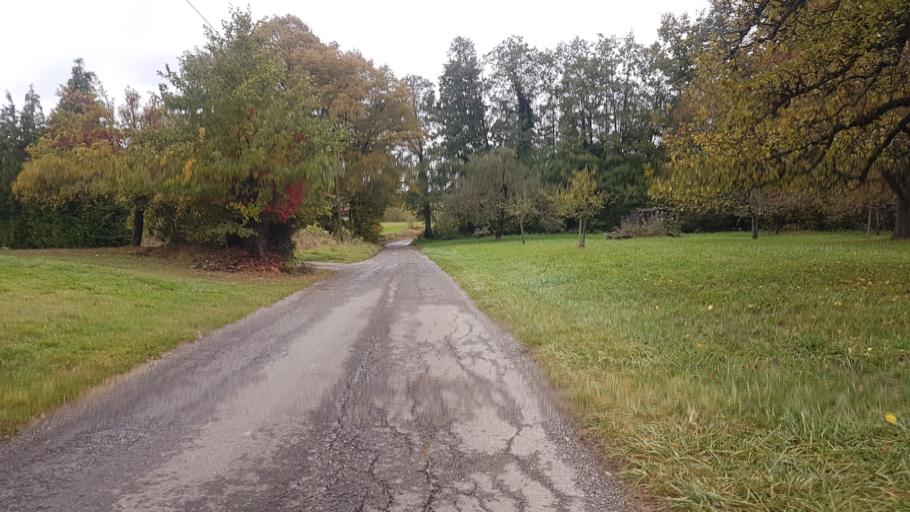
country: DE
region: Baden-Wuerttemberg
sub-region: Tuebingen Region
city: Dusslingen
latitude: 48.4630
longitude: 9.0408
